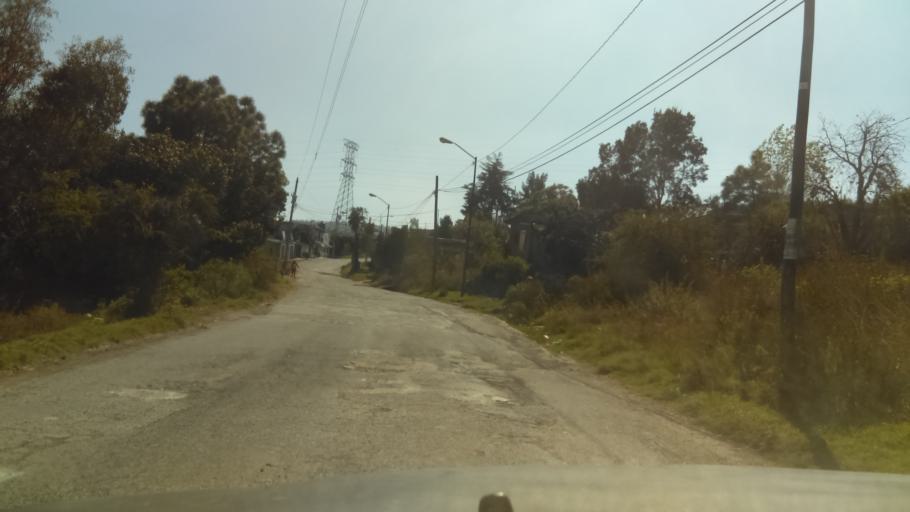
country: MX
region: Michoacan
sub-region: Morelia
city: Montana Monarca (Punta Altozano)
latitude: 19.6580
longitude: -101.1820
